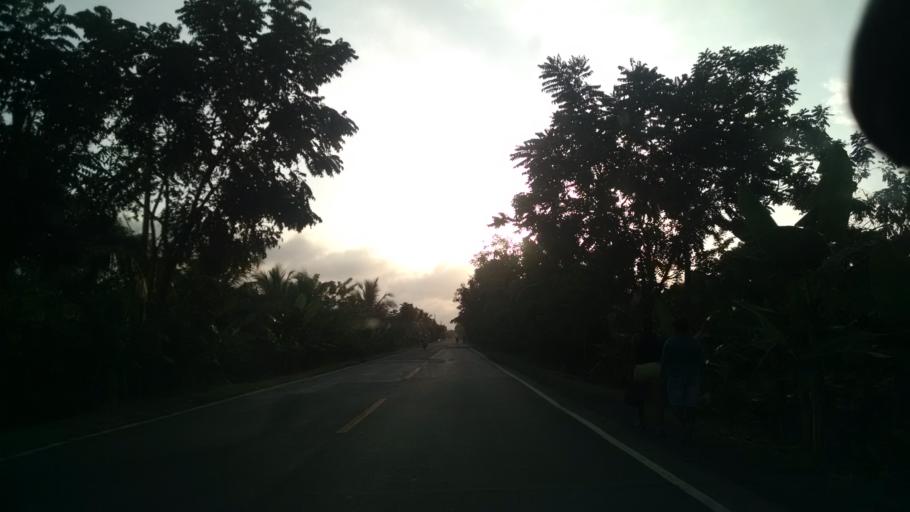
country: CO
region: Antioquia
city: San Juan de Uraba
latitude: 8.7316
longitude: -76.5803
